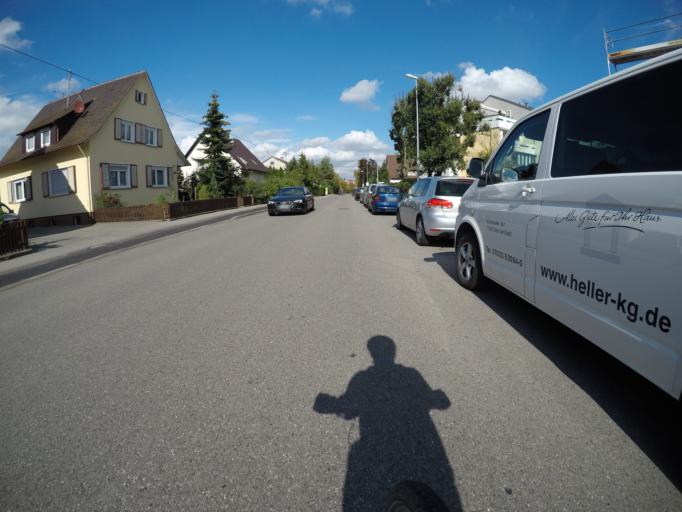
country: DE
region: Baden-Wuerttemberg
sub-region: Regierungsbezirk Stuttgart
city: Ehningen
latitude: 48.6557
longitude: 8.9333
